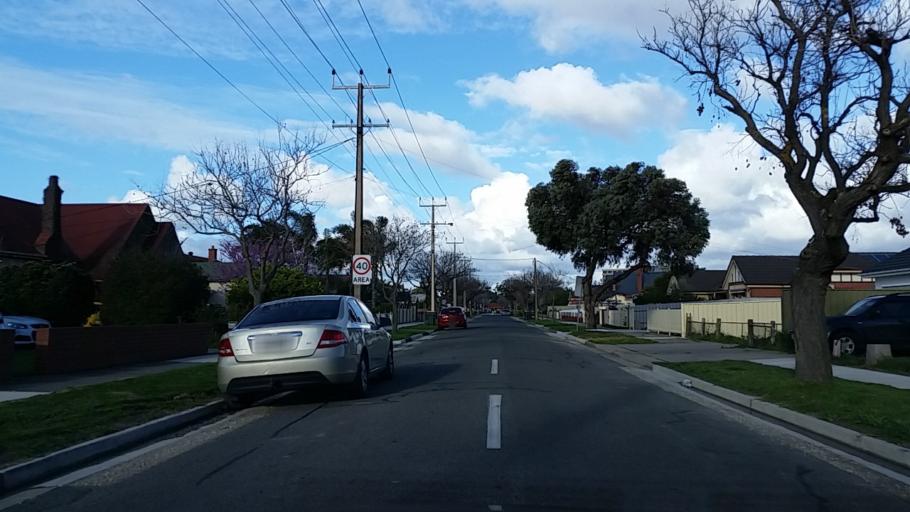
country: AU
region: South Australia
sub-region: Charles Sturt
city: Woodville West
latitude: -34.8828
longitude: 138.5262
